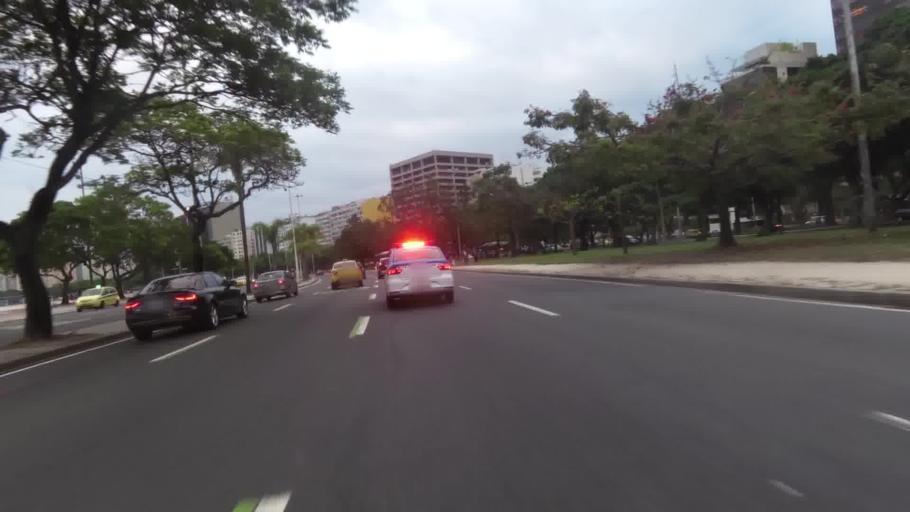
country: BR
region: Rio de Janeiro
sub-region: Rio De Janeiro
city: Rio de Janeiro
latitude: -22.9428
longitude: -43.1799
